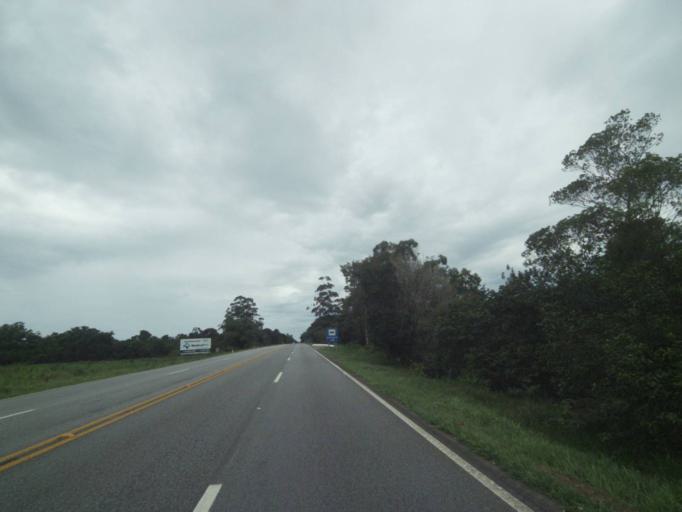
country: BR
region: Parana
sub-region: Pontal Do Parana
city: Pontal do Parana
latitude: -25.6355
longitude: -48.5934
